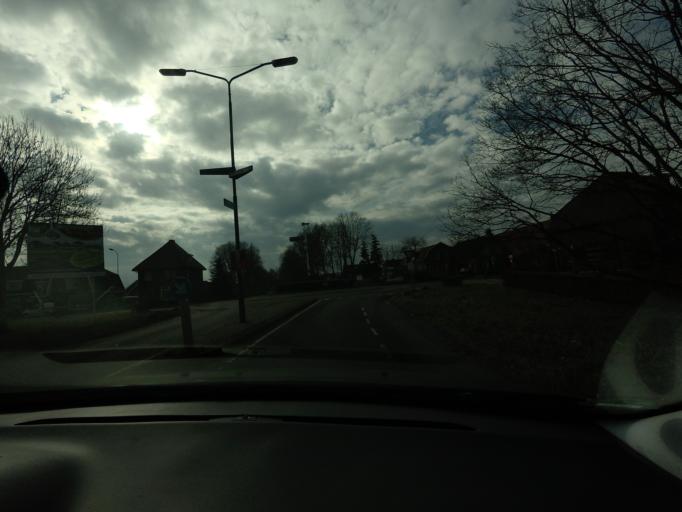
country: NL
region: North Brabant
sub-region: Gemeente Waalwijk
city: Waspik
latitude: 51.6895
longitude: 4.9484
